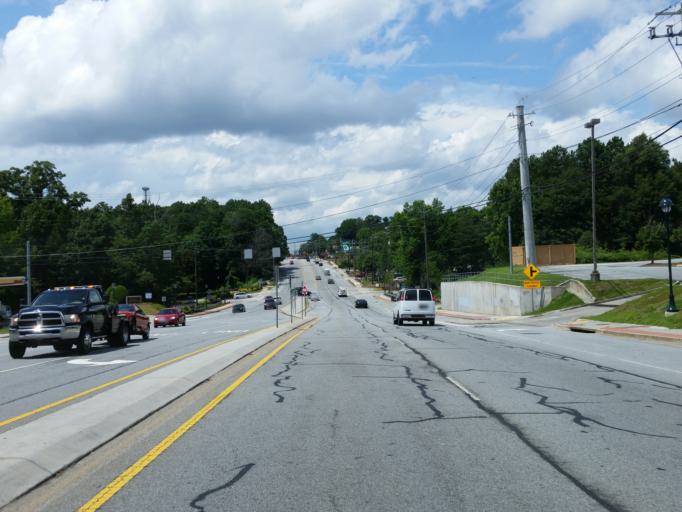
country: US
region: Georgia
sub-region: DeKalb County
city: Dunwoody
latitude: 33.9823
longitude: -84.3503
